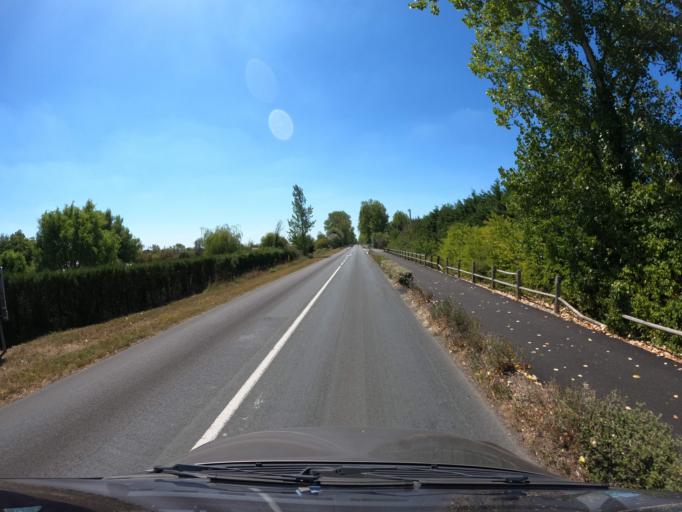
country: FR
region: Pays de la Loire
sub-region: Departement de la Vendee
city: Le Perrier
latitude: 46.8042
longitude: -2.0286
